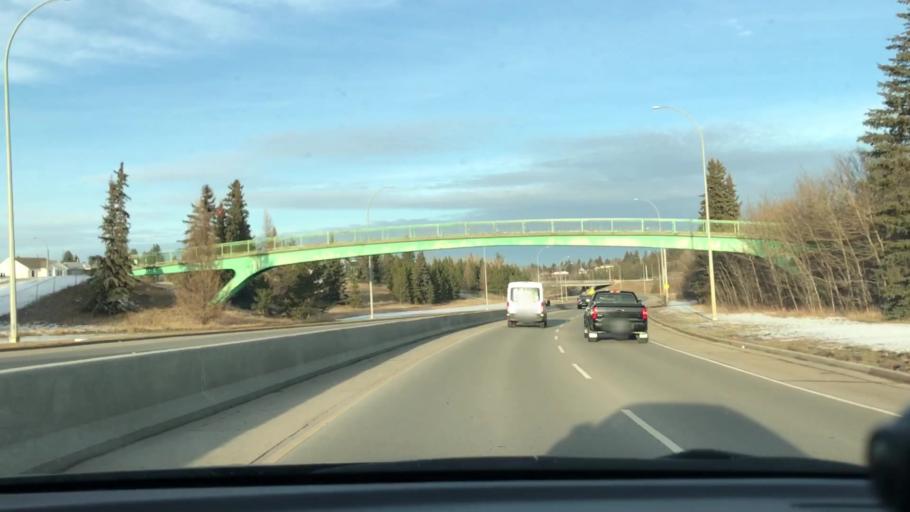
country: CA
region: Alberta
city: Edmonton
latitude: 53.5461
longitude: -113.4426
